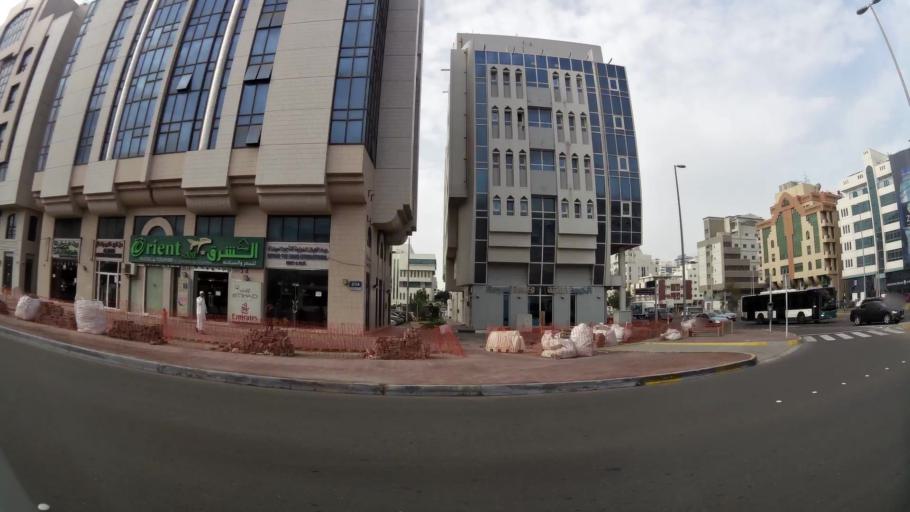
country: AE
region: Abu Dhabi
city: Abu Dhabi
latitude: 24.4612
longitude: 54.3871
